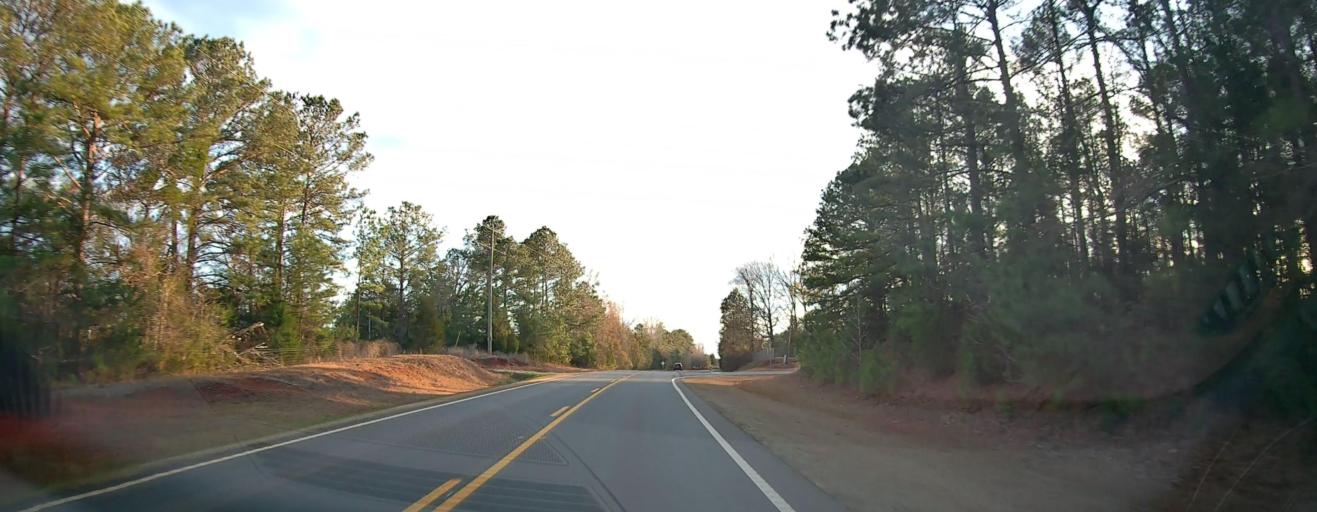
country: US
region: Georgia
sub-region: Talbot County
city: Sardis
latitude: 32.6987
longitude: -84.7005
